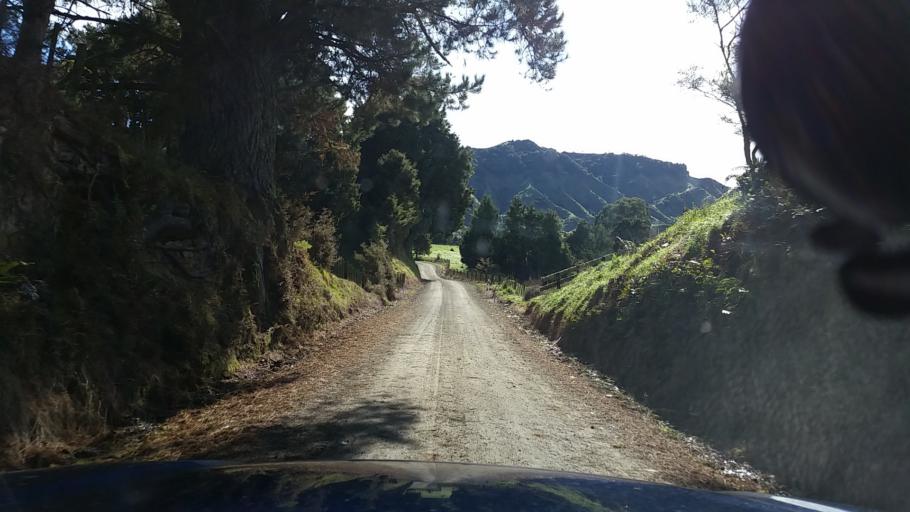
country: NZ
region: Taranaki
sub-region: New Plymouth District
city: Waitara
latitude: -39.0551
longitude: 174.7729
